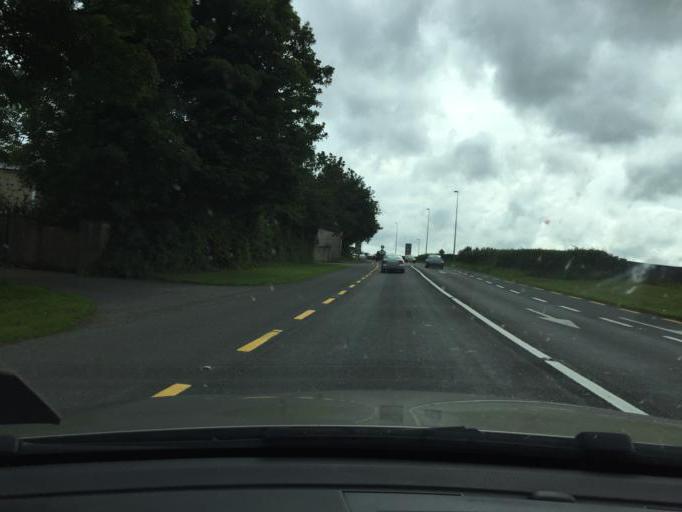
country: IE
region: Munster
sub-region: Waterford
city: Dungarvan
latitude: 52.1075
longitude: -7.6014
